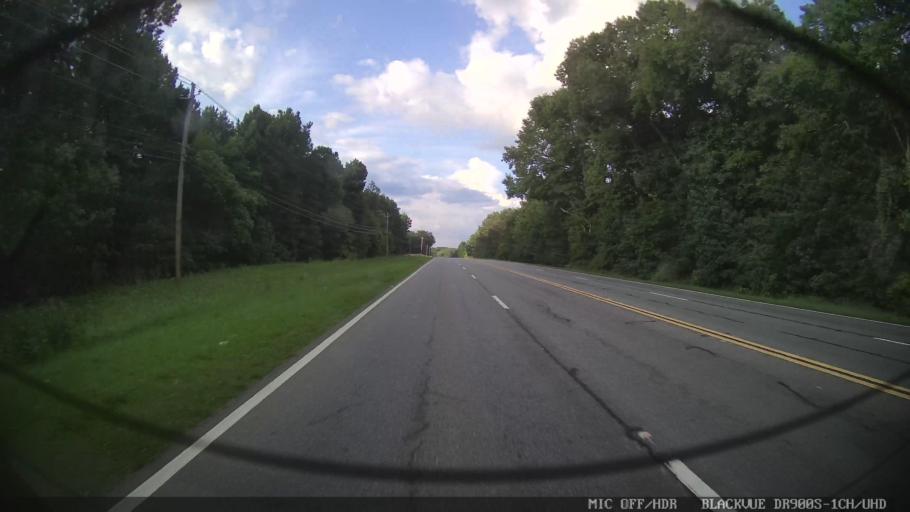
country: US
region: Georgia
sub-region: Bartow County
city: Cartersville
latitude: 34.2544
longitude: -84.7676
